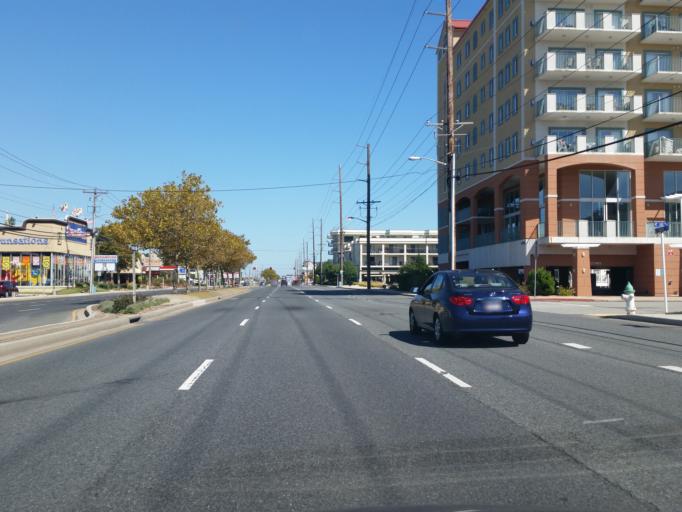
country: US
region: Delaware
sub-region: Sussex County
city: Bethany Beach
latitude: 38.4450
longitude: -75.0529
